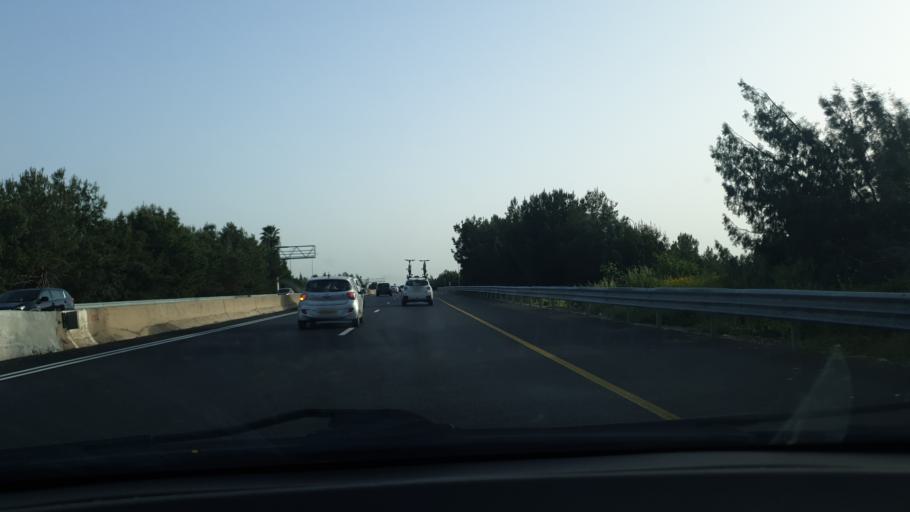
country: IL
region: Central District
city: Even Yehuda
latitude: 32.2349
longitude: 34.8850
